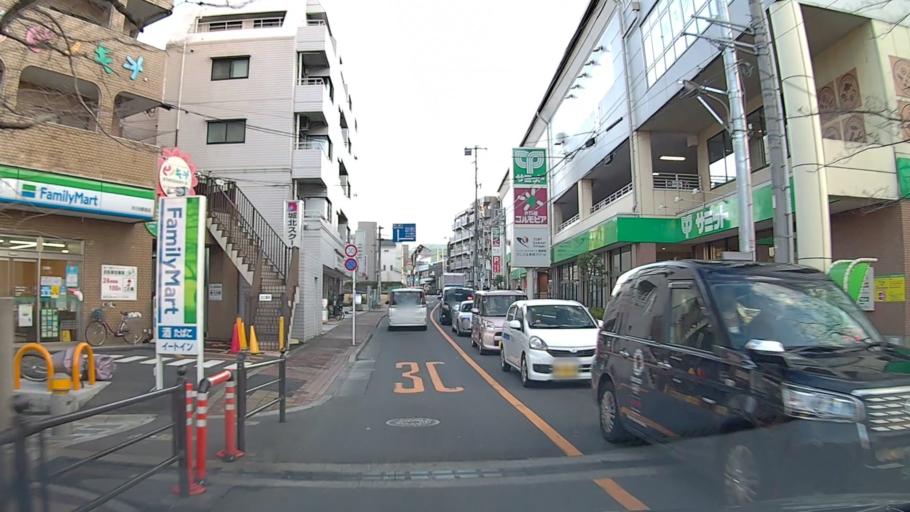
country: JP
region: Saitama
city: Wako
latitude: 35.7490
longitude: 139.6664
